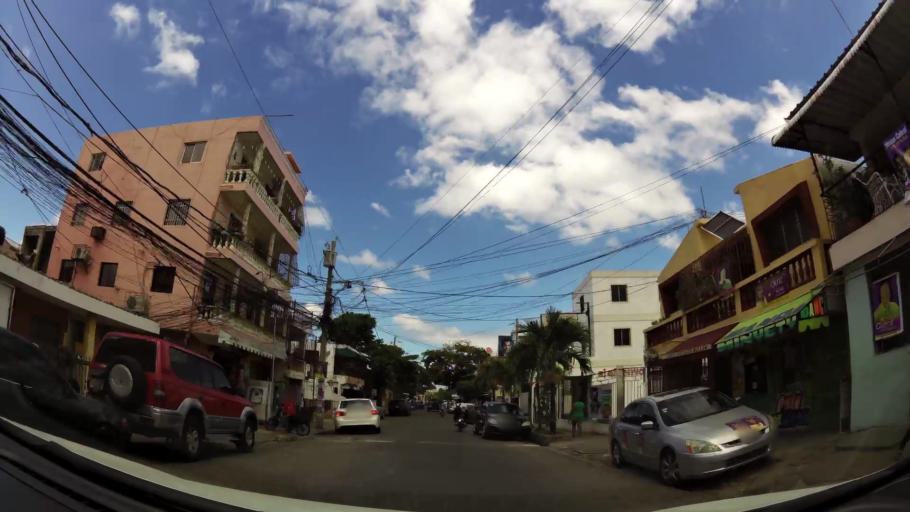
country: DO
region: Nacional
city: Bella Vista
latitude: 18.4665
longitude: -69.9474
